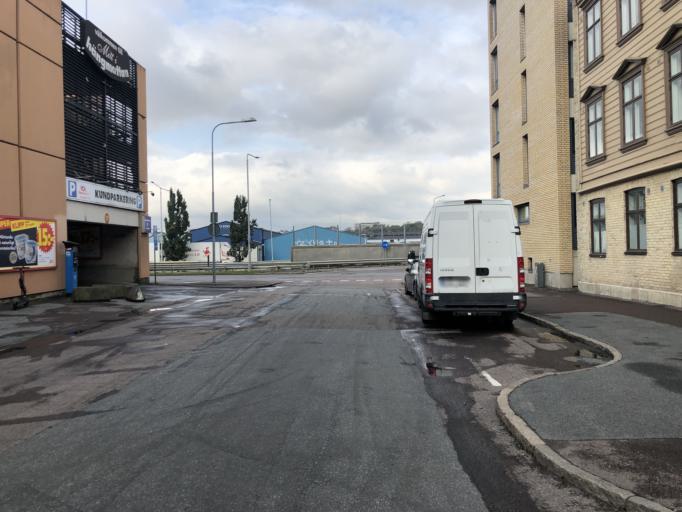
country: SE
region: Vaestra Goetaland
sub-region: Goteborg
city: Majorna
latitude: 57.6975
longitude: 11.9285
